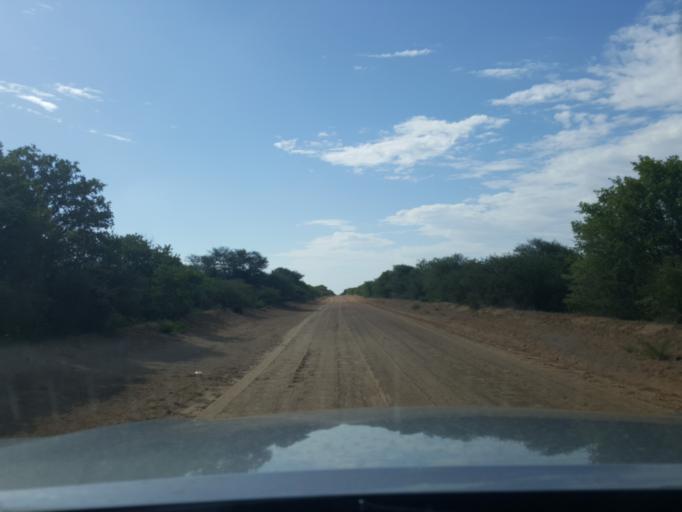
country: BW
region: Kweneng
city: Khudumelapye
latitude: -23.5167
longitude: 24.7167
